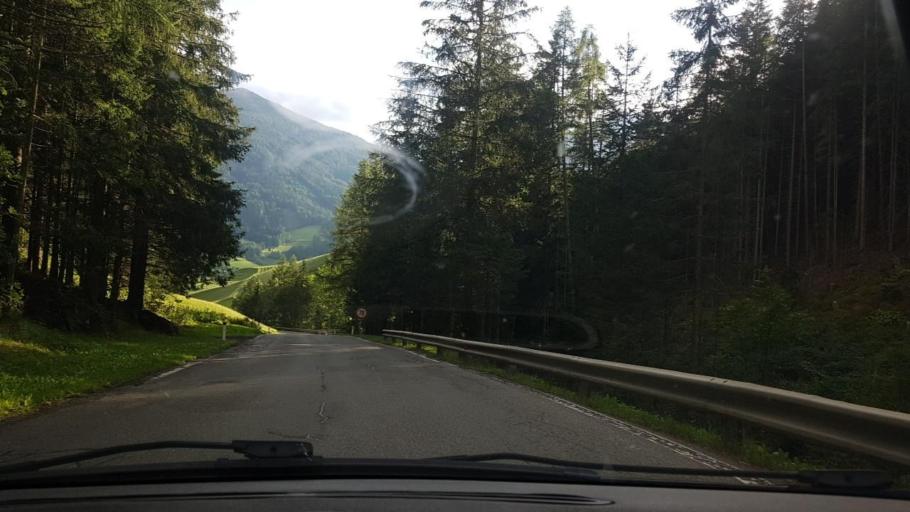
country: AT
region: Salzburg
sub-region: Politischer Bezirk Tamsweg
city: Sankt Michael im Lungau
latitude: 47.0366
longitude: 13.6072
